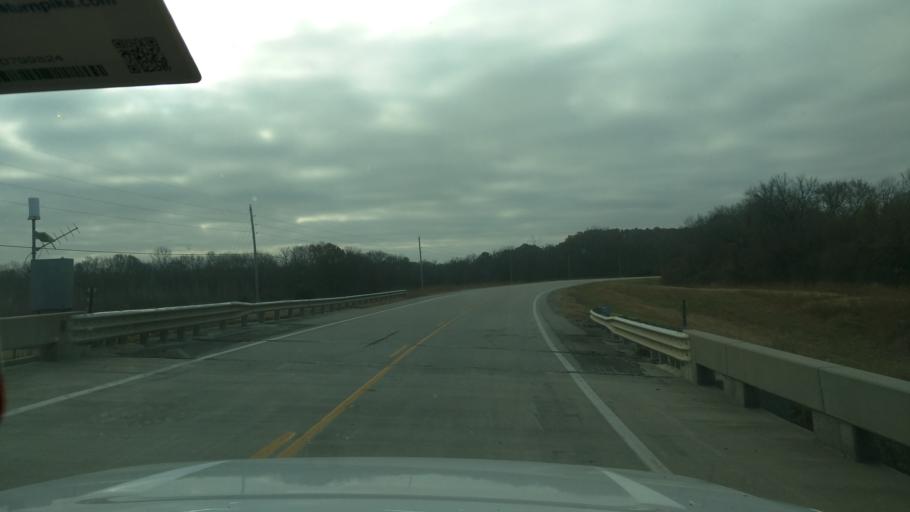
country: US
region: Kansas
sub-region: Greenwood County
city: Eureka
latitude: 37.7085
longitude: -96.2237
